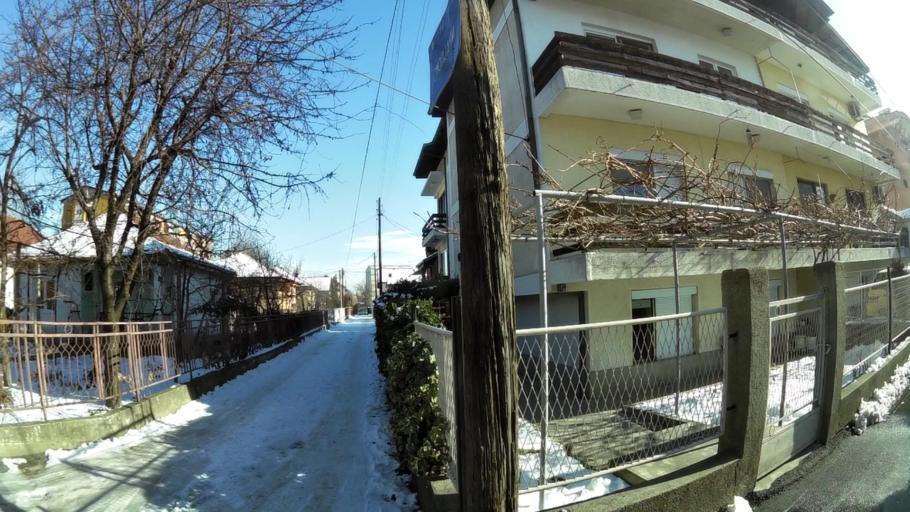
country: MK
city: Krushopek
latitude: 42.0059
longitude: 21.3567
